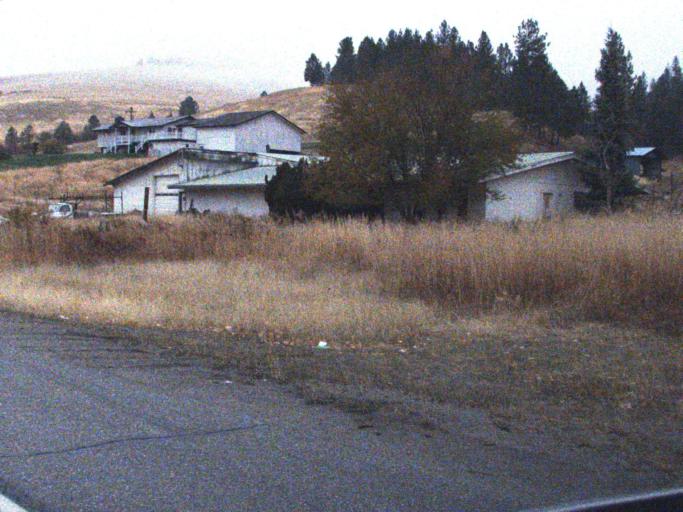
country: US
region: Washington
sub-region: Stevens County
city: Kettle Falls
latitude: 48.5956
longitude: -118.0026
